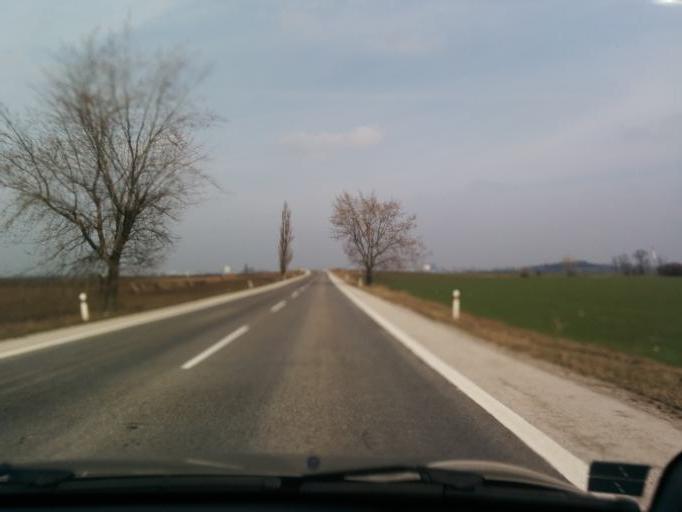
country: SK
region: Trnavsky
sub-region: Okres Galanta
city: Galanta
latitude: 48.2531
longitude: 17.7089
